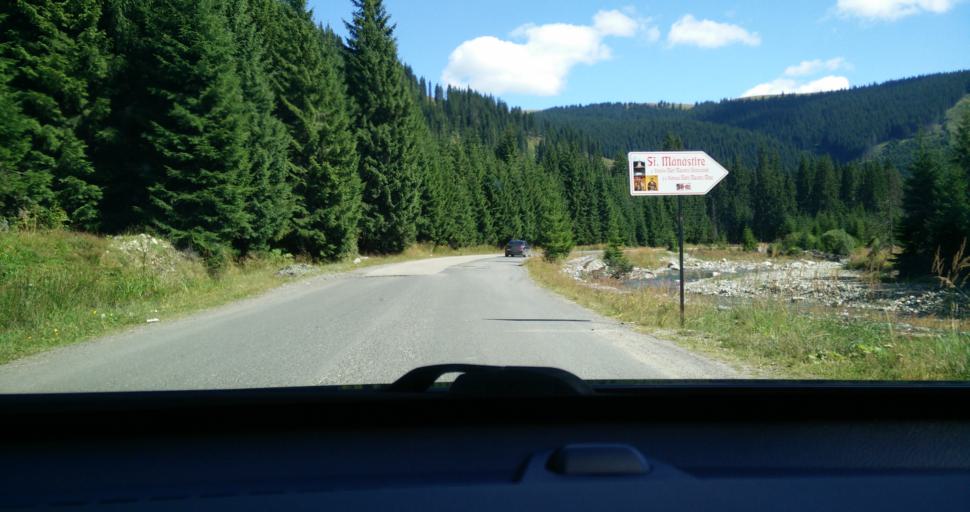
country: RO
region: Hunedoara
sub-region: Oras Petrila
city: Petrila
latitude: 45.4301
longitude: 23.6206
